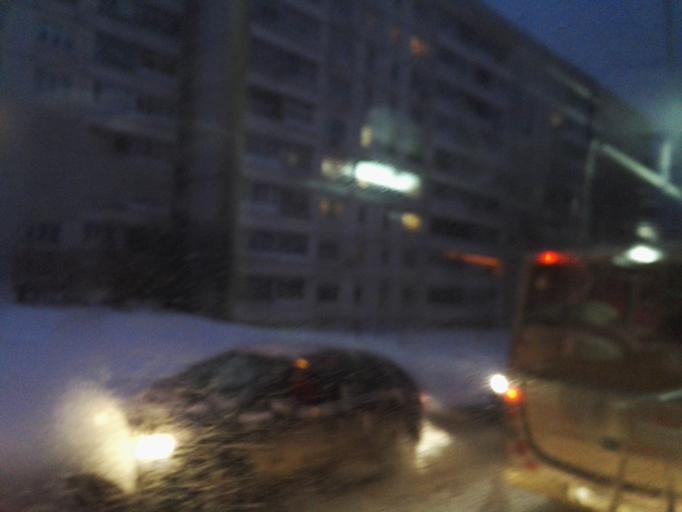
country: RU
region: Tula
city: Mendeleyevskiy
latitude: 54.1600
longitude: 37.6020
